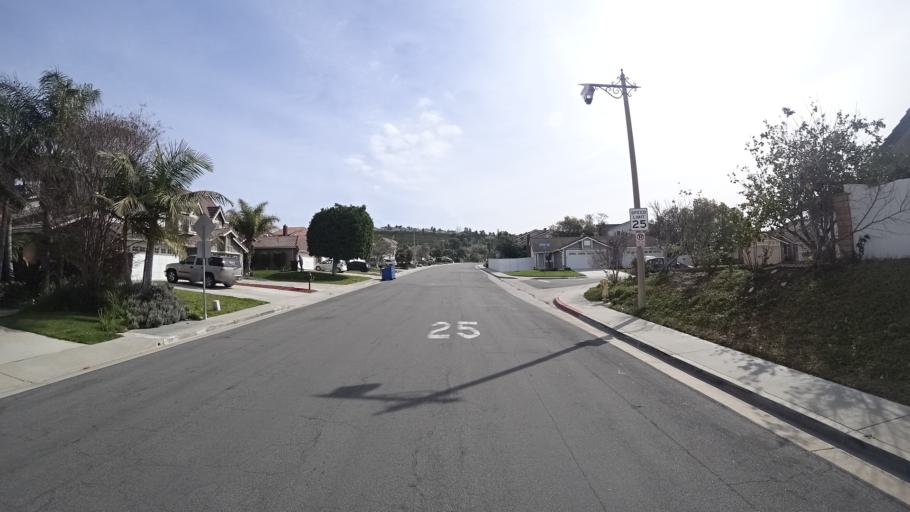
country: US
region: California
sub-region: Orange County
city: Yorba Linda
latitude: 33.8691
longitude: -117.7383
